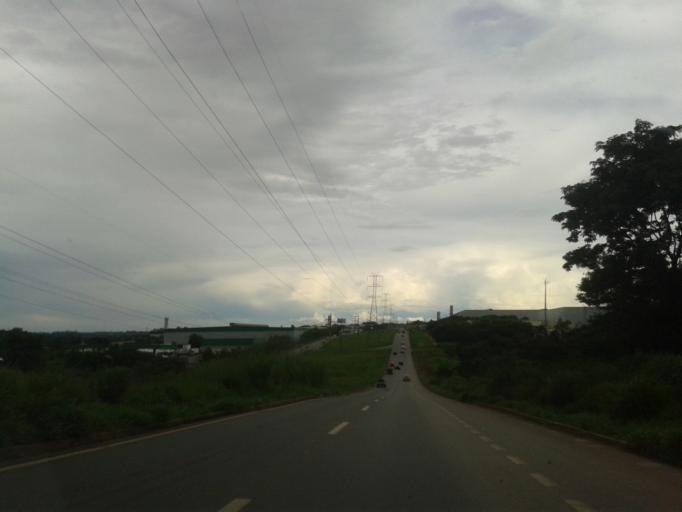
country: BR
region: Goias
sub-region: Aparecida De Goiania
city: Aparecida de Goiania
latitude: -16.7859
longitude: -49.2607
